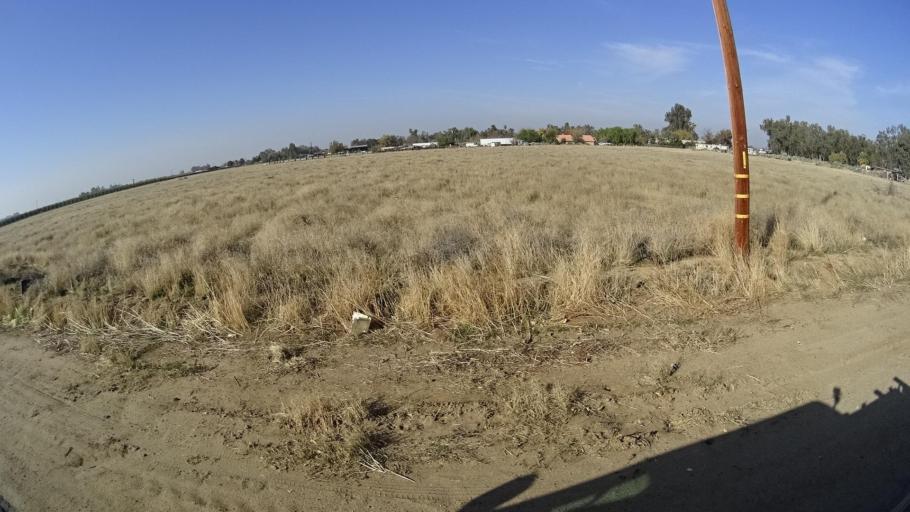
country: US
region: California
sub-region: Kern County
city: Lamont
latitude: 35.3314
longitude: -118.8961
